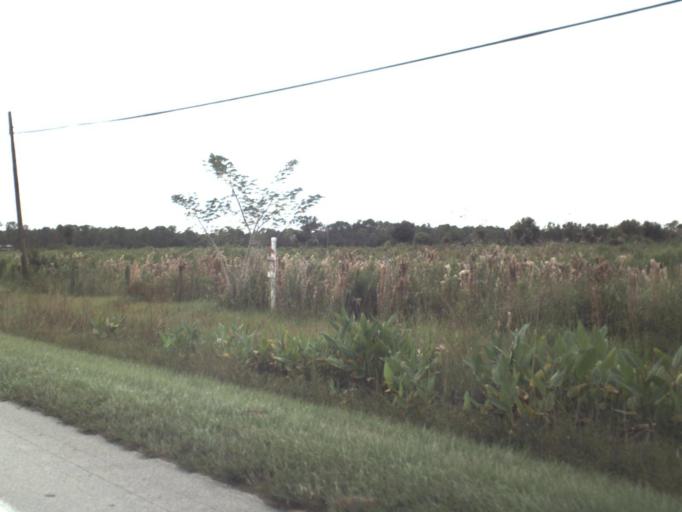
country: US
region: Florida
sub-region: Lee County
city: Fort Myers Shores
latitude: 26.7641
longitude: -81.7609
